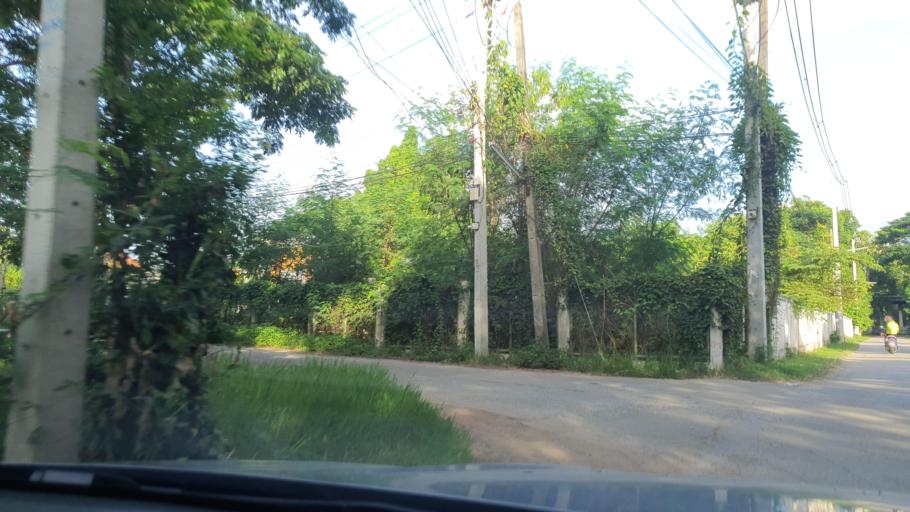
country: TH
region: Chiang Mai
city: San Kamphaeng
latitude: 18.7510
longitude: 99.1139
